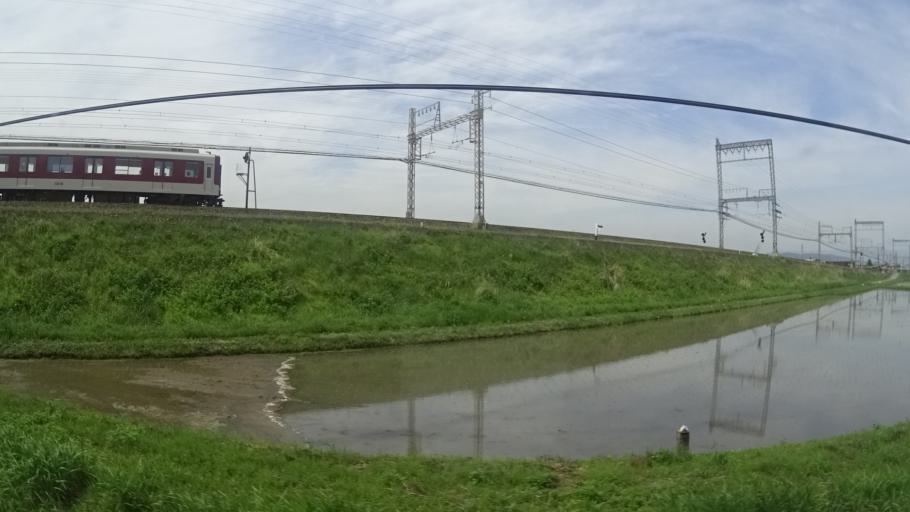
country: JP
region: Mie
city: Hisai-motomachi
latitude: 34.6062
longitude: 136.5086
